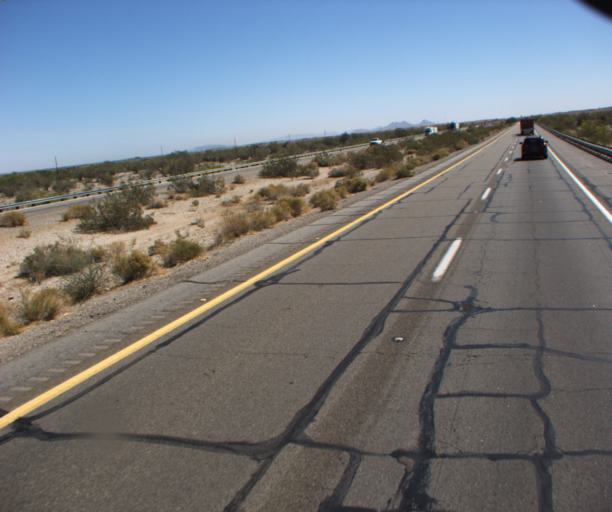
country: US
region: Arizona
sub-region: Yuma County
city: Wellton
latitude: 32.6606
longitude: -114.2580
